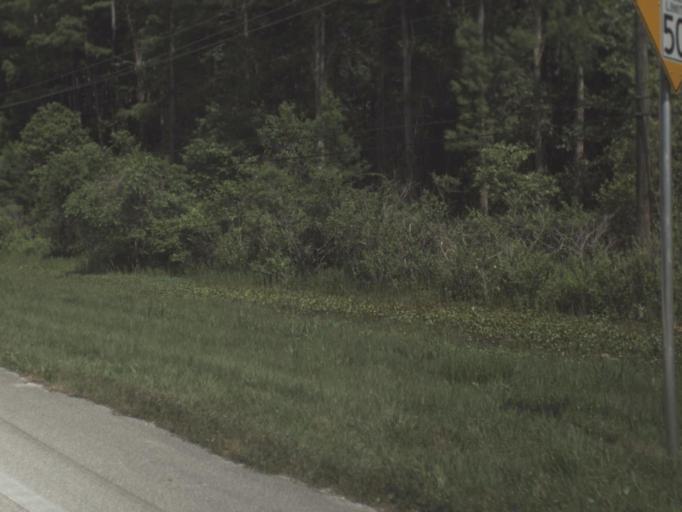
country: US
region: Florida
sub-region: Saint Johns County
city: Butler Beach
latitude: 29.7567
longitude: -81.3003
